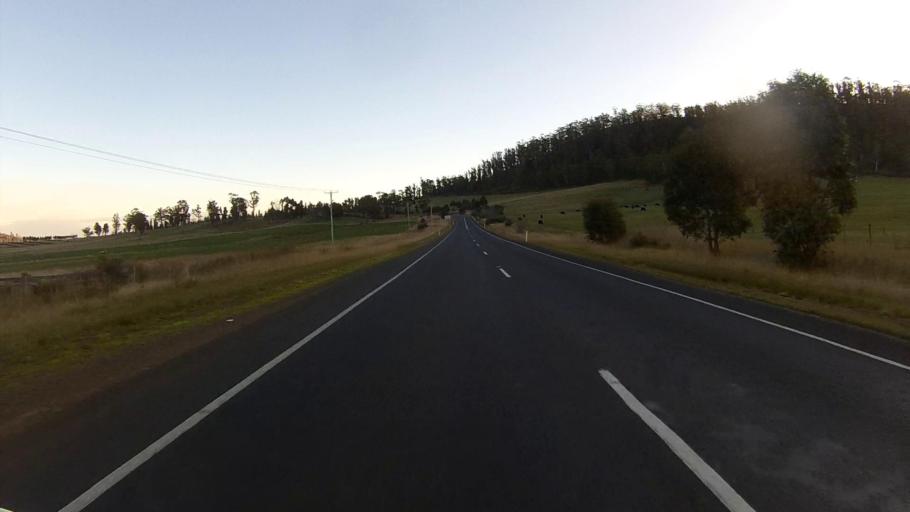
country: AU
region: Tasmania
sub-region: Sorell
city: Sorell
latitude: -42.8193
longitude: 147.7471
